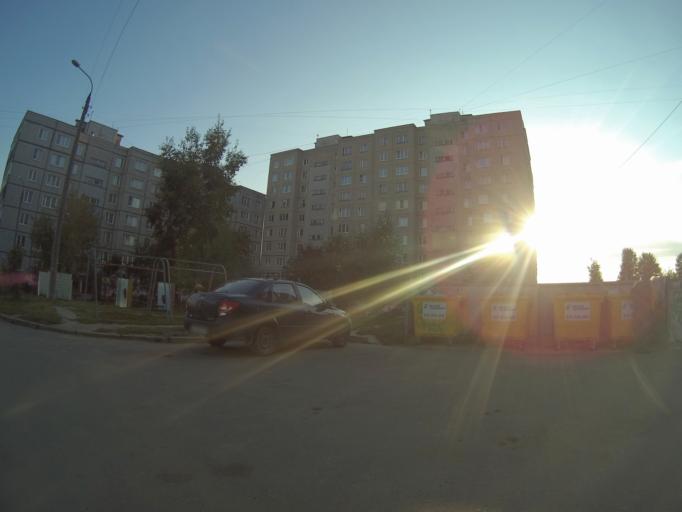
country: RU
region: Vladimir
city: Vladimir
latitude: 56.1028
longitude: 40.3488
